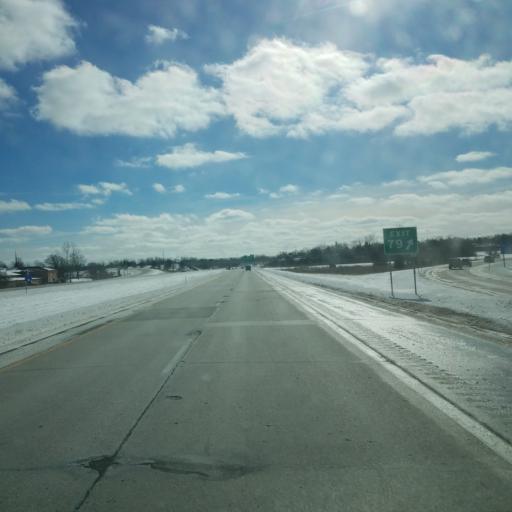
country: US
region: Michigan
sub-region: Ingham County
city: East Lansing
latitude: 42.7646
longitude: -84.5111
